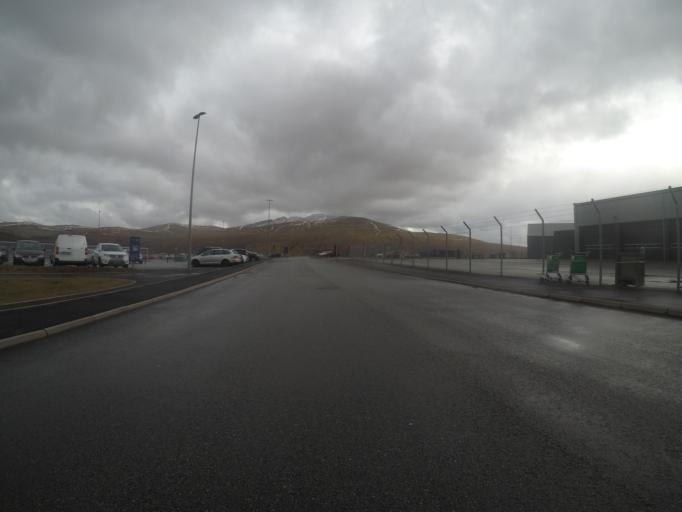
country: FO
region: Vagar
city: Midvagur
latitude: 62.0674
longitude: -7.2769
